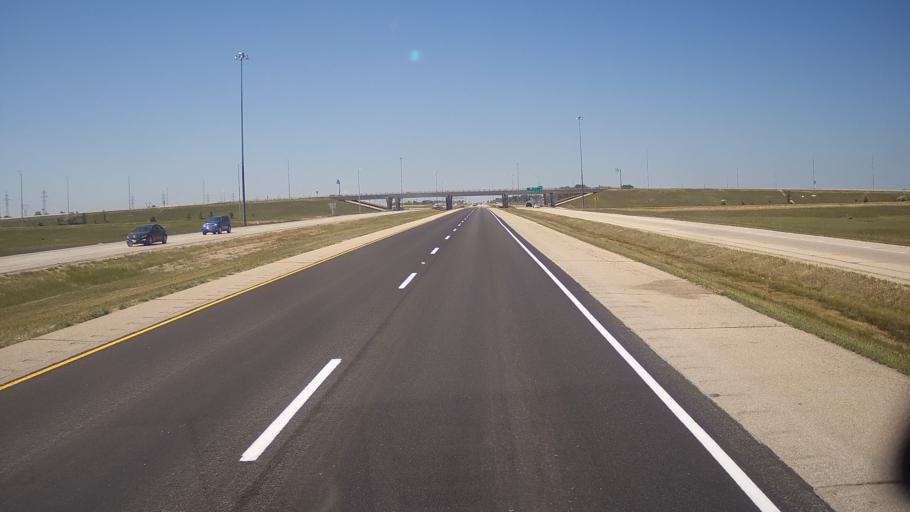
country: CA
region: Manitoba
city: Winnipeg
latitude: 49.9900
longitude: -97.2242
